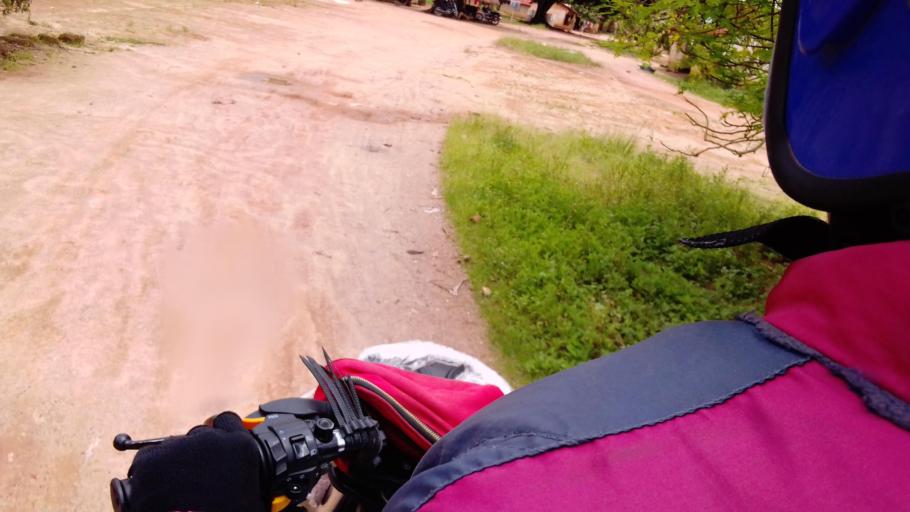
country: SL
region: Eastern Province
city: Koidu
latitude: 8.6779
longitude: -10.9579
